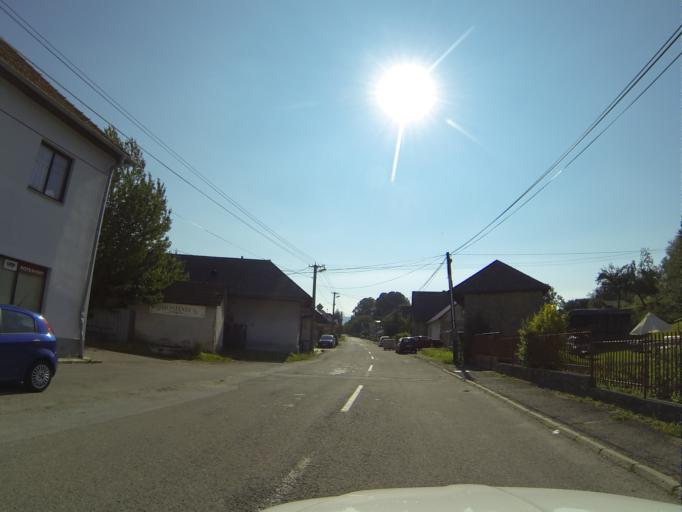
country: SK
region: Nitriansky
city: Prievidza
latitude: 48.7768
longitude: 18.6993
